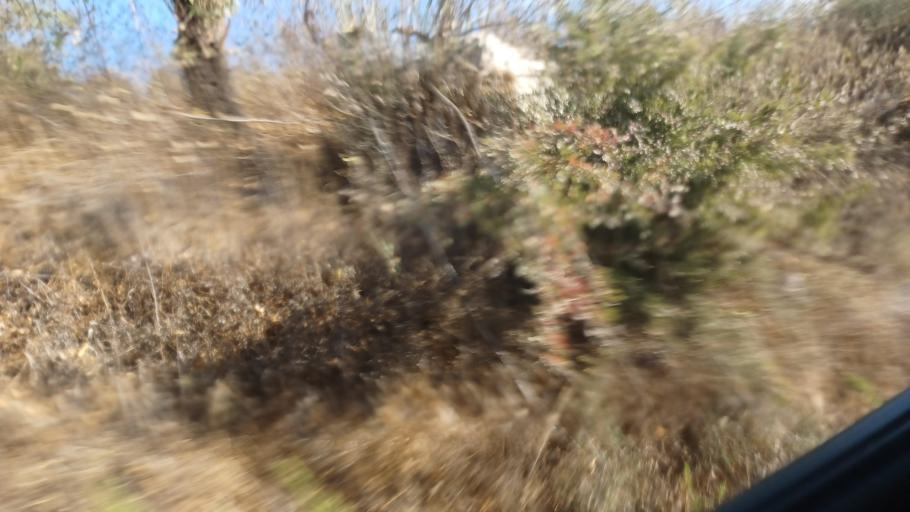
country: CY
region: Pafos
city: Mesogi
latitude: 34.8560
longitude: 32.4751
